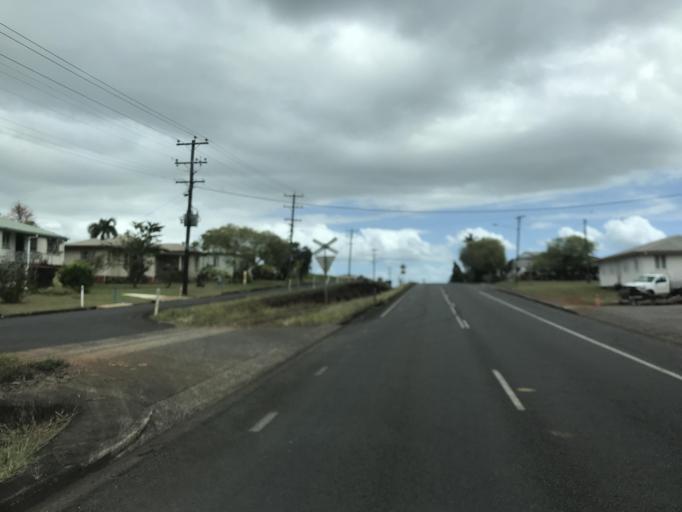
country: AU
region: Queensland
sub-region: Cassowary Coast
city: Innisfail
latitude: -17.5965
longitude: 145.9961
